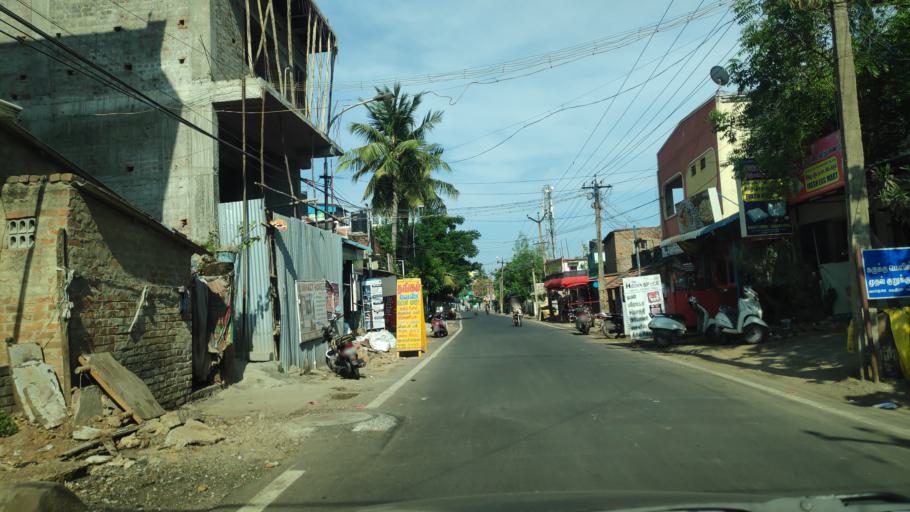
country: IN
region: Tamil Nadu
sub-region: Thiruvallur
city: Ambattur
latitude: 13.1224
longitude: 80.1616
